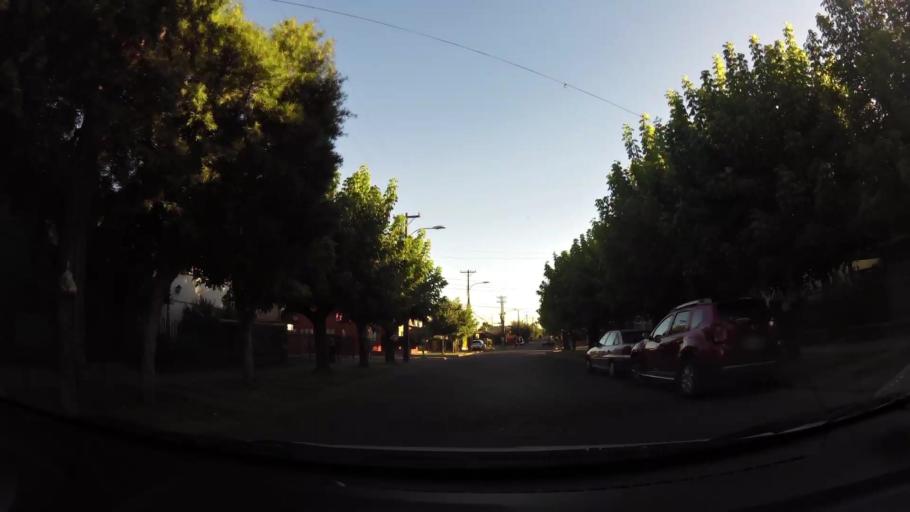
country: CL
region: Maule
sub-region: Provincia de Curico
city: Curico
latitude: -34.9939
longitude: -71.2390
